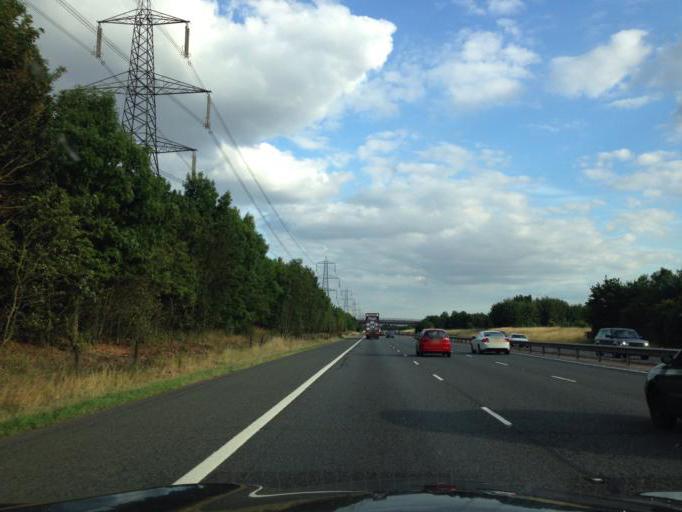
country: GB
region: England
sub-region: Oxfordshire
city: Wheatley
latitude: 51.8022
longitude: -1.0932
